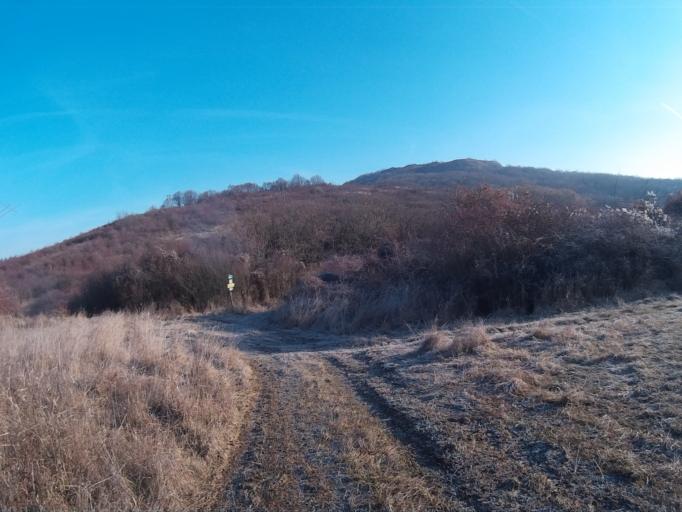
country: HU
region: Nograd
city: Bercel
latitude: 47.9130
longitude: 19.3936
